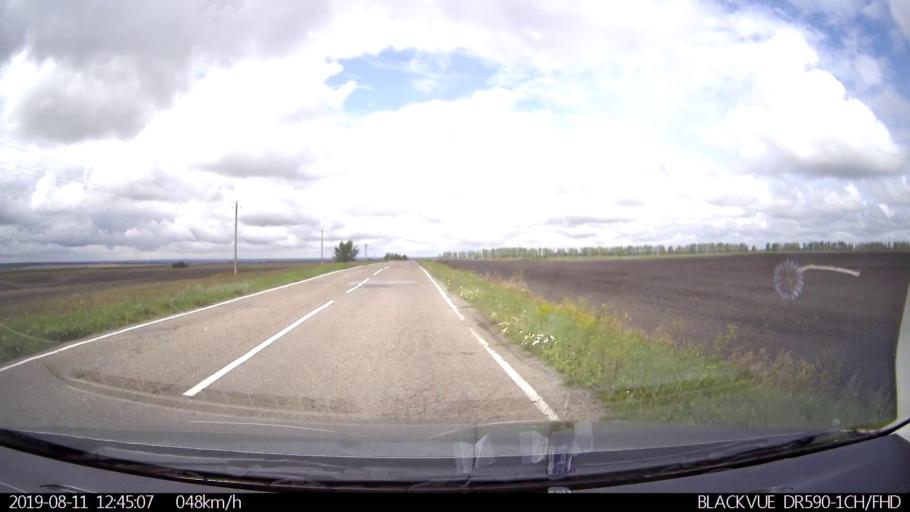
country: RU
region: Ulyanovsk
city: Ignatovka
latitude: 53.8579
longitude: 47.7308
